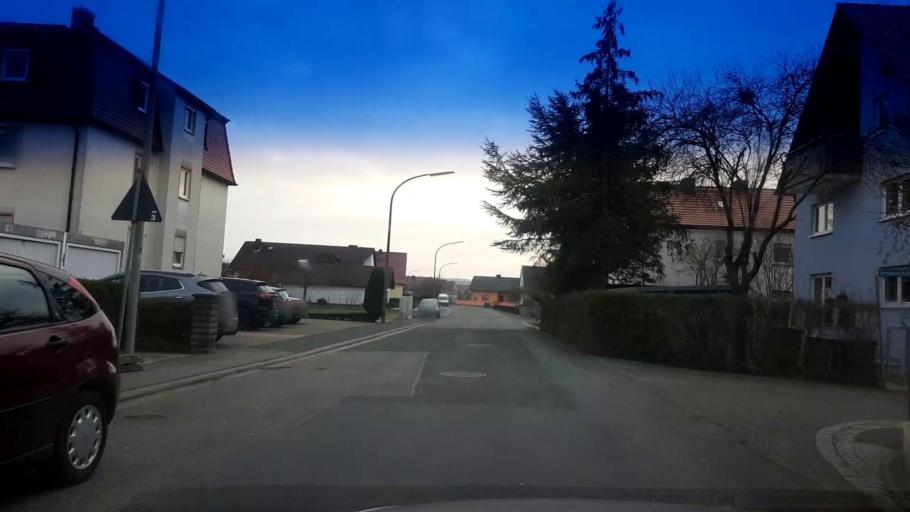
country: DE
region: Bavaria
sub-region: Upper Franconia
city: Hirschaid
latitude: 49.8210
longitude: 10.9846
